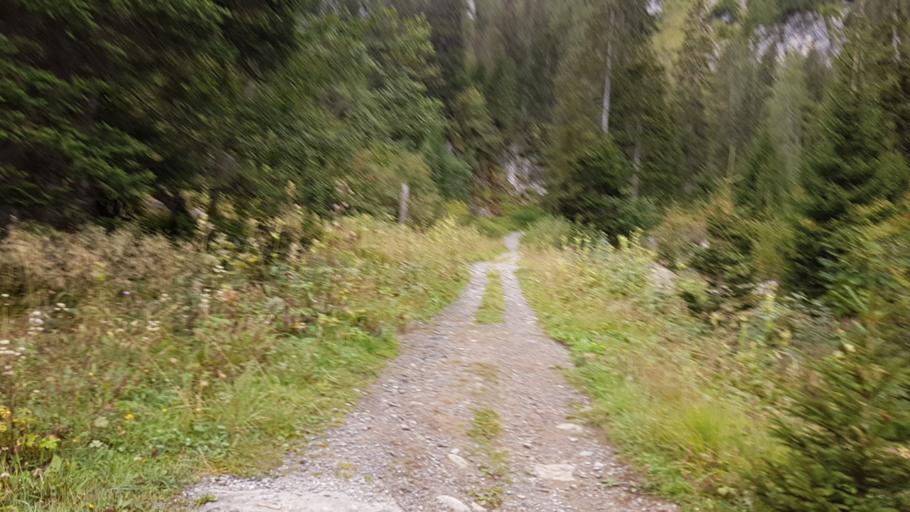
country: CH
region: Bern
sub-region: Frutigen-Niedersimmental District
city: Kandersteg
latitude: 46.4700
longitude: 7.6554
